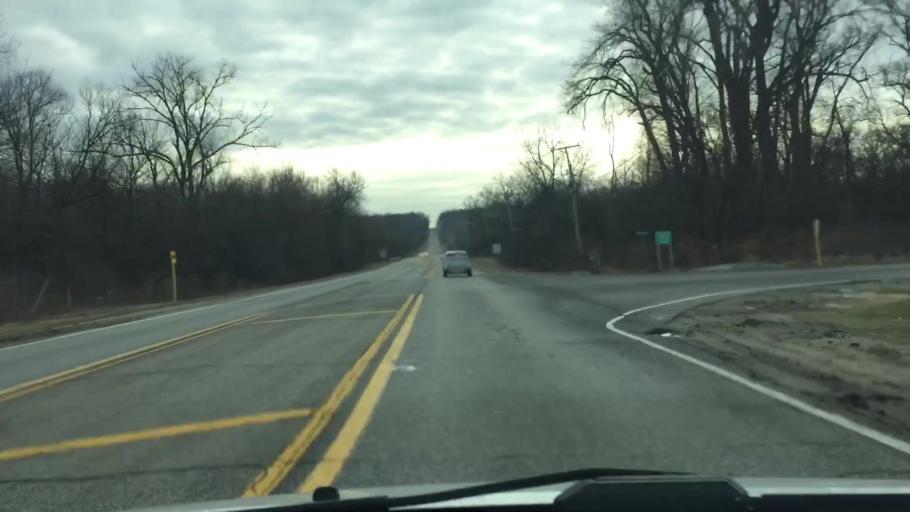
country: US
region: Illinois
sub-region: McHenry County
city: Prairie Grove
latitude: 42.2725
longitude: -88.2869
